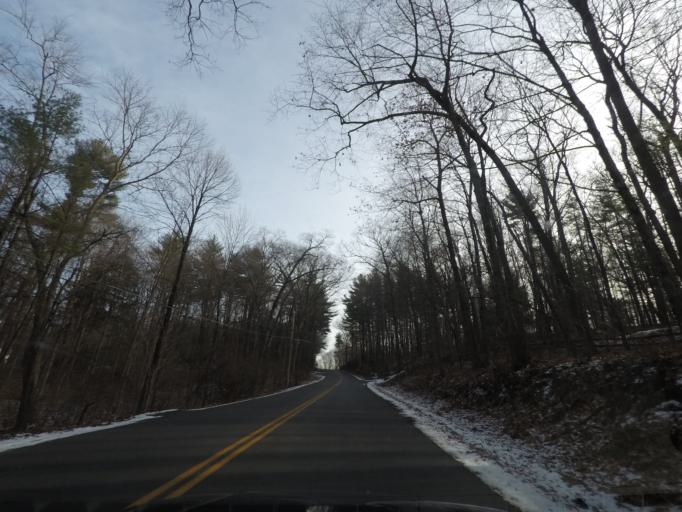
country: US
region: New York
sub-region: Saratoga County
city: Stillwater
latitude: 42.9897
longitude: -73.7217
